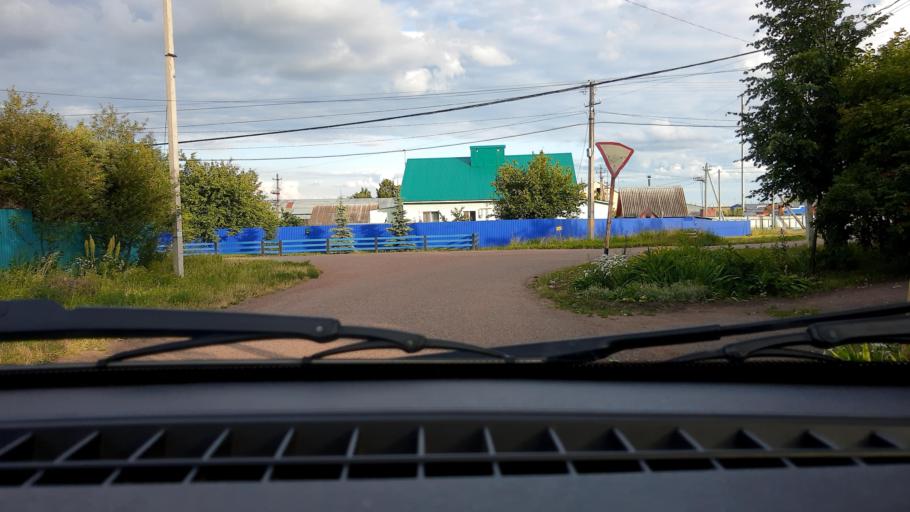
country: RU
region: Bashkortostan
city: Mikhaylovka
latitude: 54.8066
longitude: 55.7963
